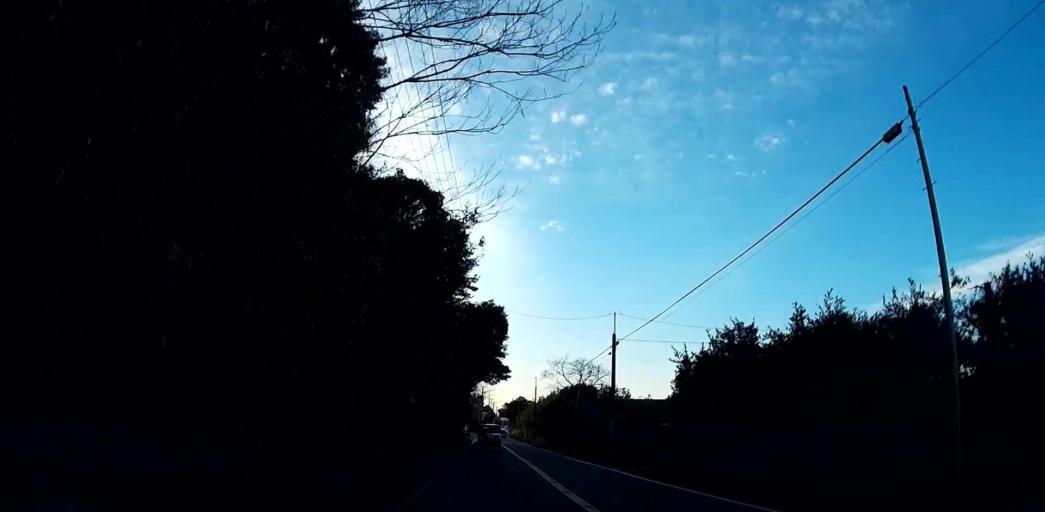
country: JP
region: Chiba
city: Omigawa
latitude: 35.8463
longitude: 140.6313
